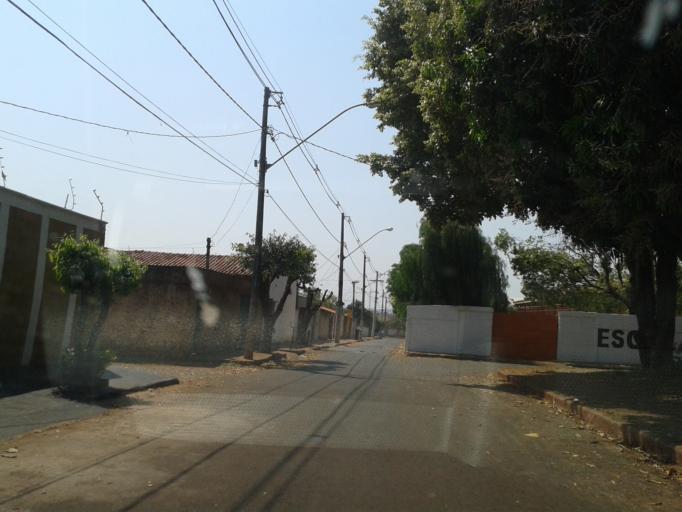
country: BR
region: Minas Gerais
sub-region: Ituiutaba
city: Ituiutaba
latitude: -18.9634
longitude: -49.4515
